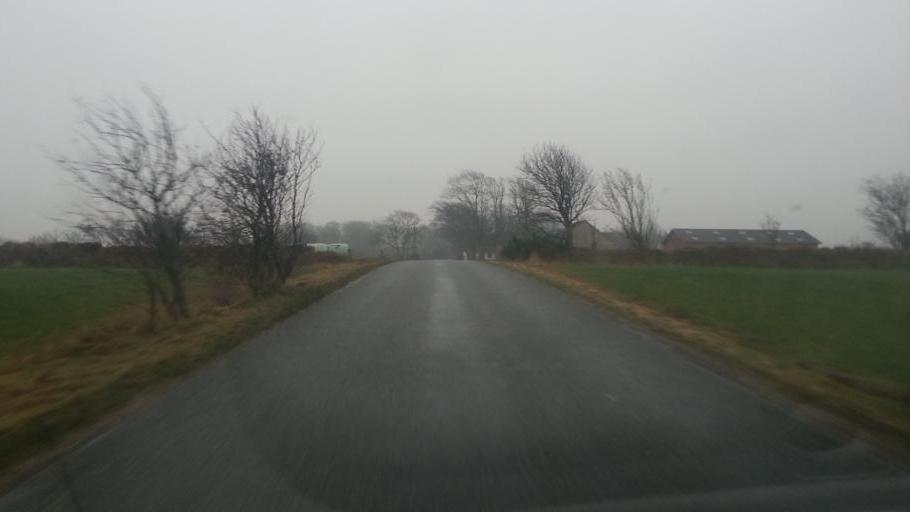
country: DK
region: South Denmark
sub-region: Esbjerg Kommune
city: Tjaereborg
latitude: 55.4751
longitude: 8.6161
